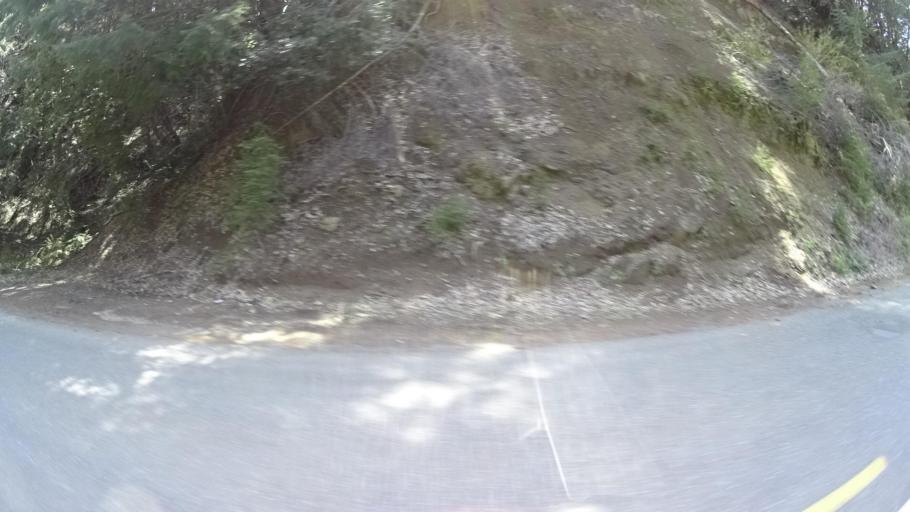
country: US
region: California
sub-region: Humboldt County
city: Rio Dell
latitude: 40.2850
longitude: -124.0593
